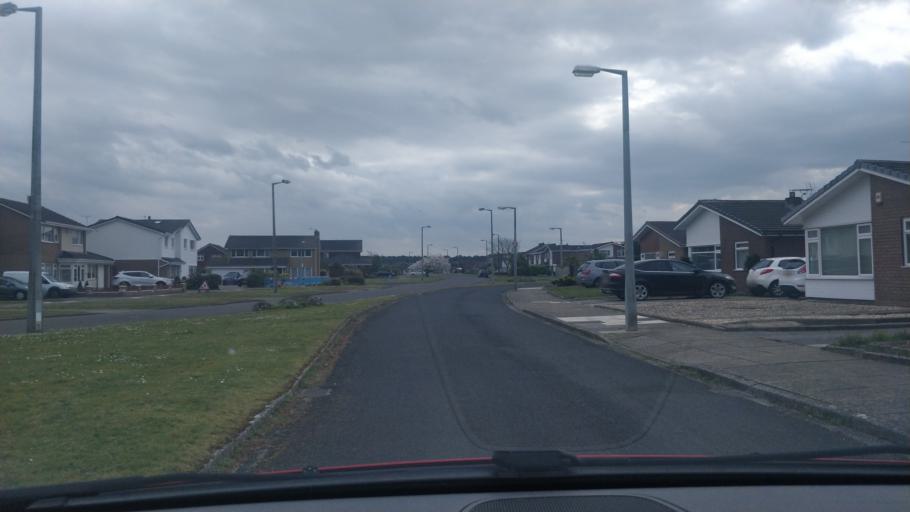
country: GB
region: England
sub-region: Sefton
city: Formby
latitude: 53.6036
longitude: -3.0532
